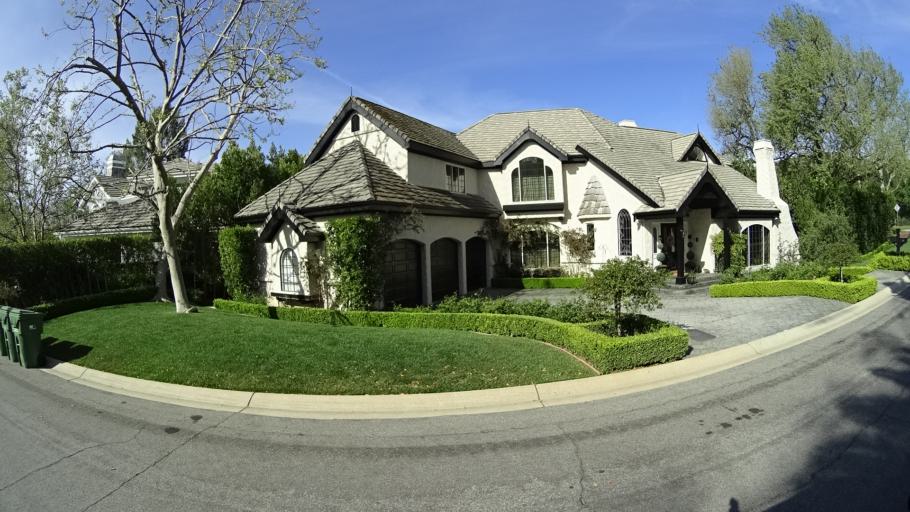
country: US
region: California
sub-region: Ventura County
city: Oak Park
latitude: 34.1919
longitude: -118.7920
